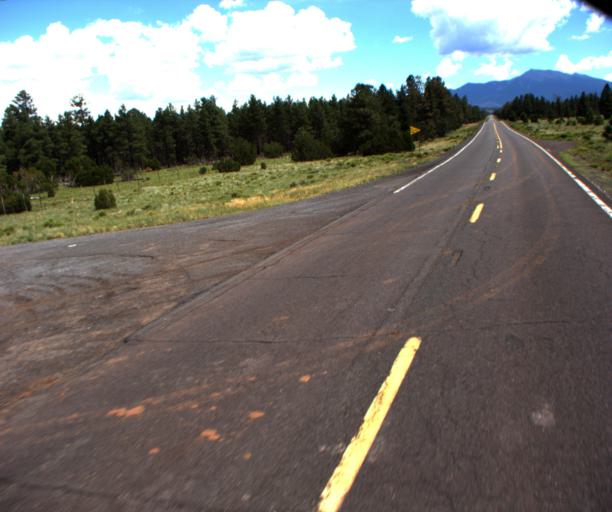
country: US
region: Arizona
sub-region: Coconino County
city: Parks
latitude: 35.4887
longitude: -111.8084
